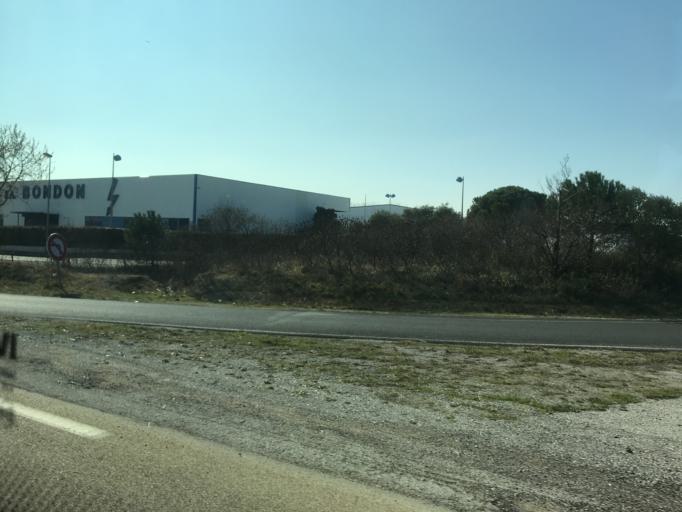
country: FR
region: Languedoc-Roussillon
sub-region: Departement de l'Herault
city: Perols
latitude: 43.5924
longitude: 3.9403
